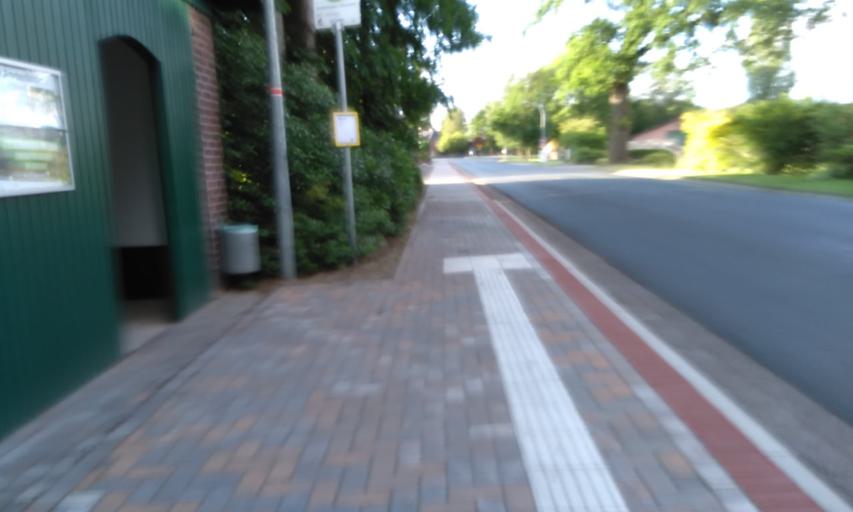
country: DE
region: Lower Saxony
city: Anderlingen
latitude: 53.3732
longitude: 9.3023
